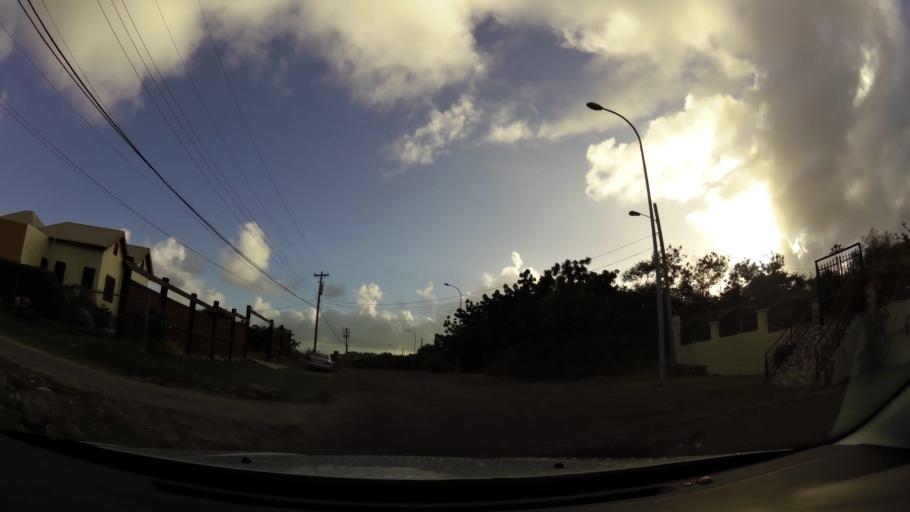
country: AG
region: Saint John
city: Saint John's
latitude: 17.1520
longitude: -61.8293
